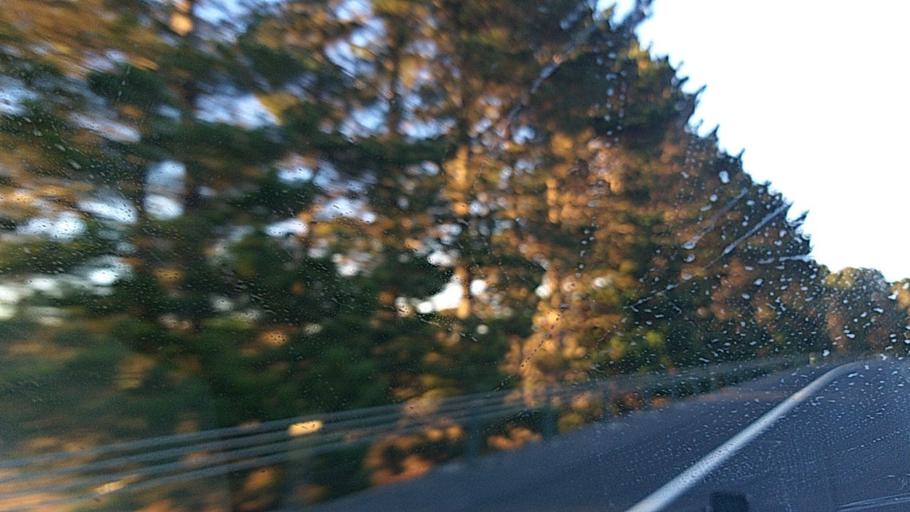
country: AU
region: New South Wales
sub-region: Goulburn Mulwaree
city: Goulburn
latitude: -34.8896
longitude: 149.5285
